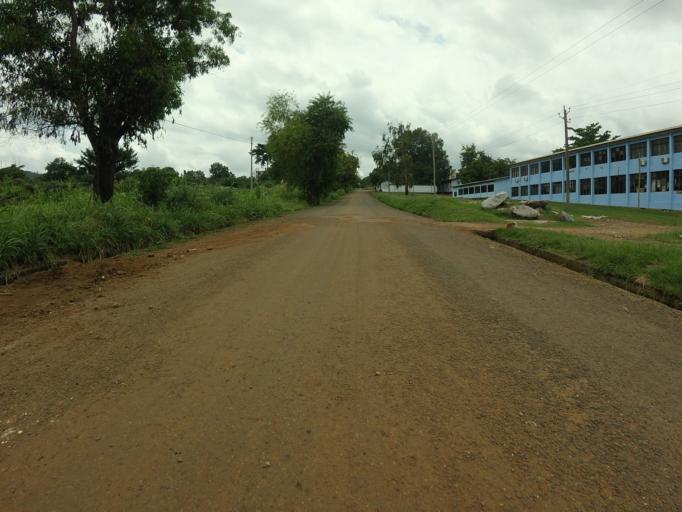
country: GH
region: Volta
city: Ho
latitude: 6.5984
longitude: 0.4590
